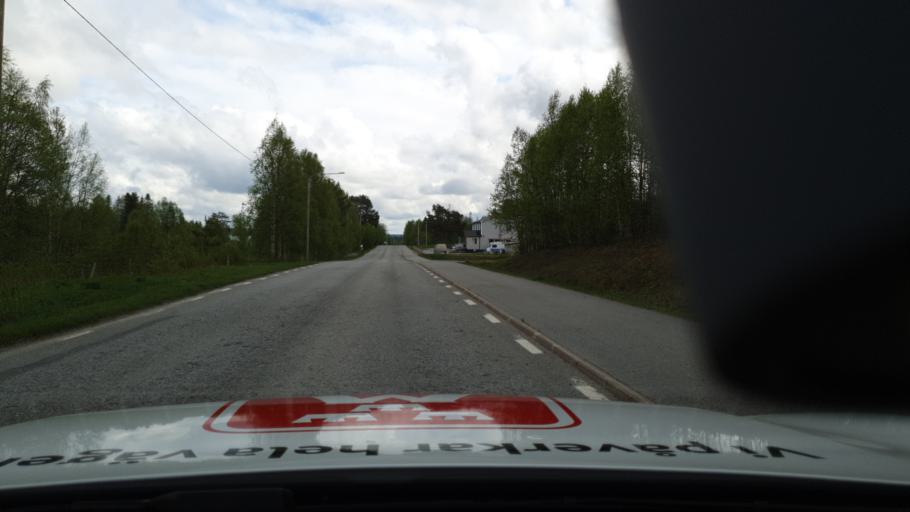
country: SE
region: Vaesterbotten
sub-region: Vilhelmina Kommun
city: Sjoberg
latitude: 64.6392
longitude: 16.3615
